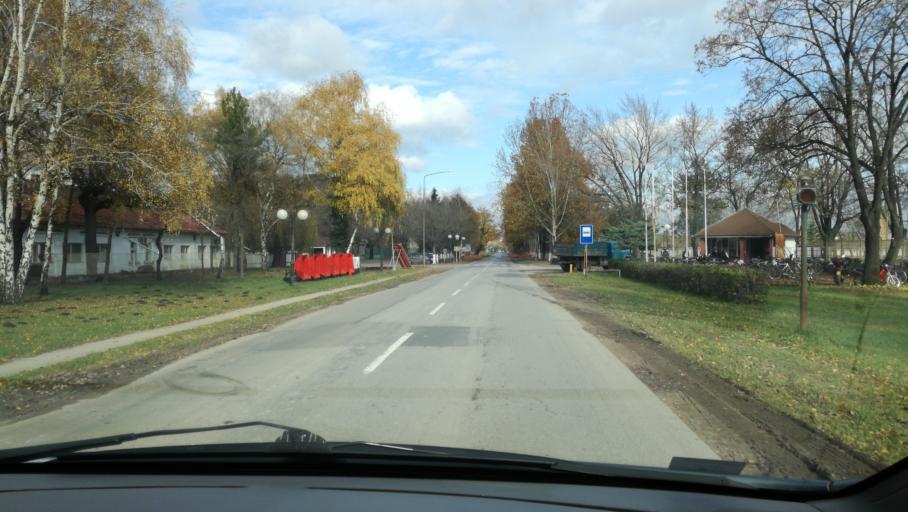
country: RS
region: Autonomna Pokrajina Vojvodina
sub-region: Severnobanatski Okrug
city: Kikinda
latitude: 45.8093
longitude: 20.4467
